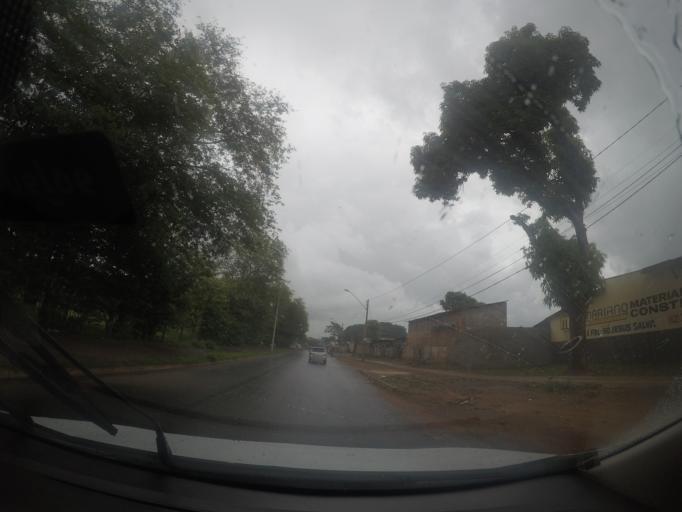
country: BR
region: Goias
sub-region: Trindade
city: Trindade
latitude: -16.6474
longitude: -49.3894
